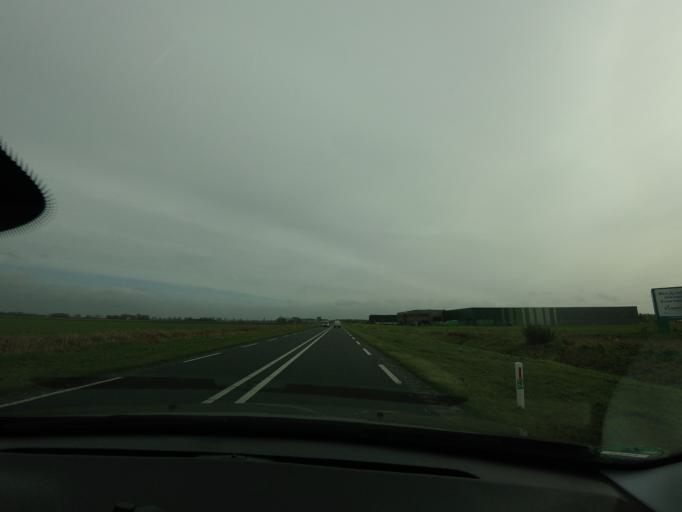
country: NL
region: Flevoland
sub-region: Gemeente Noordoostpolder
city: Emmeloord
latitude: 52.7184
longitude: 5.7861
